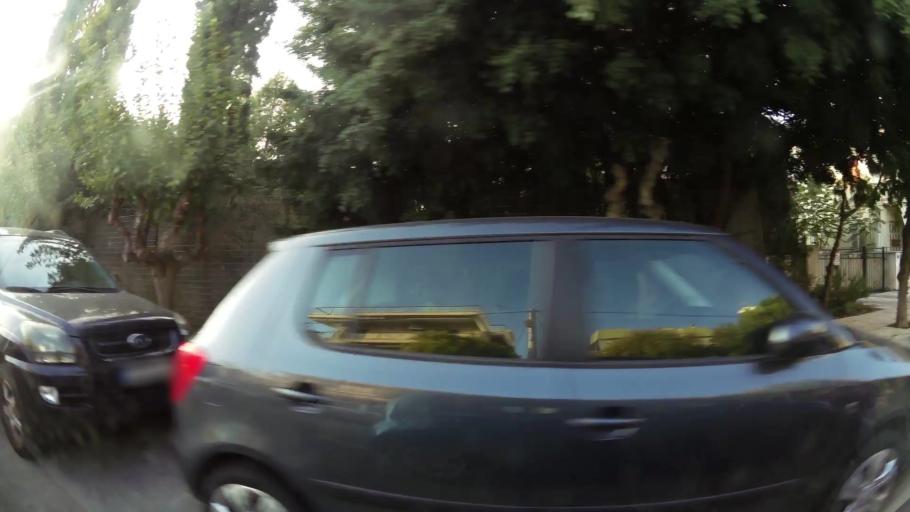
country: GR
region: Attica
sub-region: Nomarchia Athinas
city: Khalandrion
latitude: 38.0138
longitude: 23.8148
